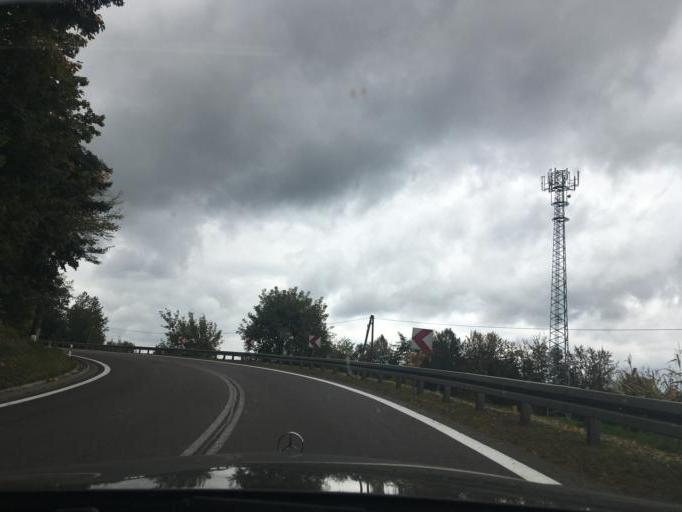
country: PL
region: Subcarpathian Voivodeship
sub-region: Powiat brzozowski
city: Jablonica Polska
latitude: 49.7249
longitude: 21.9094
